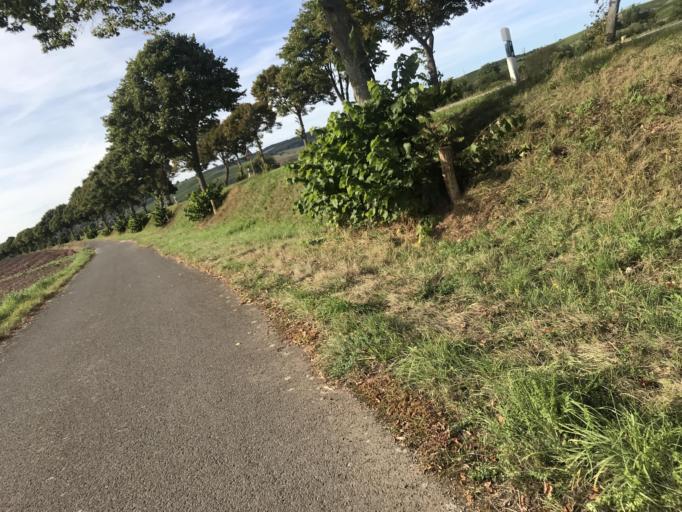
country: DE
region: Rheinland-Pfalz
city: Monzingen
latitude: 49.7908
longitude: 7.5762
